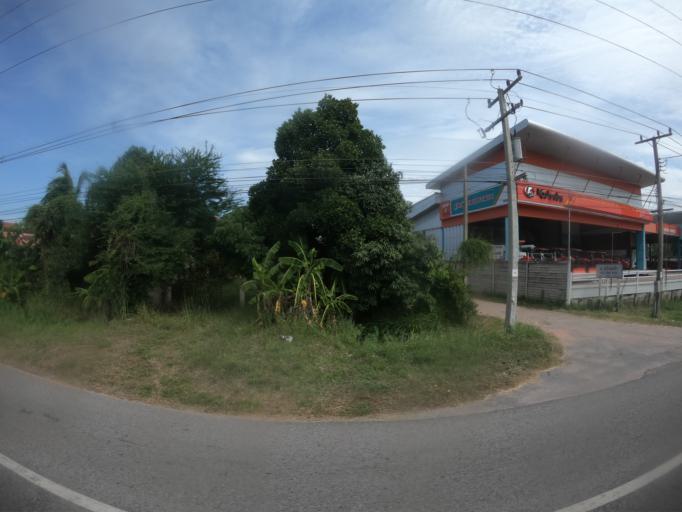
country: TH
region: Maha Sarakham
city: Chiang Yuen
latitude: 16.4231
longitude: 103.0719
